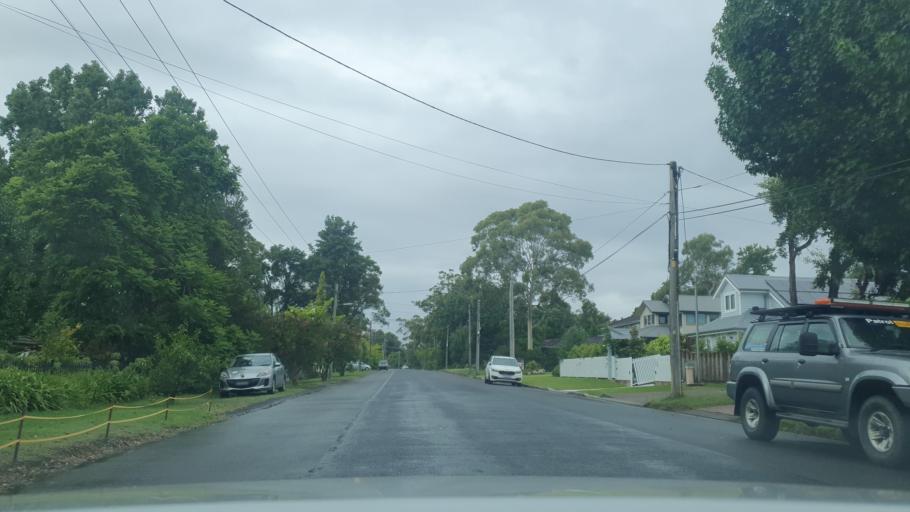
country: AU
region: New South Wales
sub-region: Blue Mountains Municipality
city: Glenbrook
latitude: -33.7728
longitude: 150.6288
